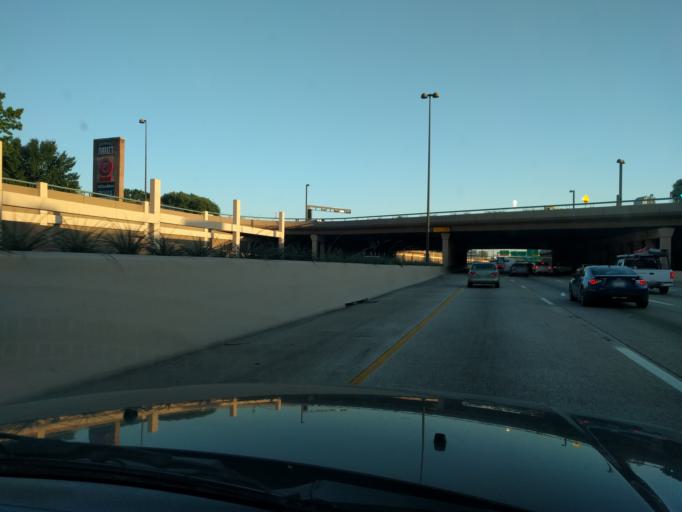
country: US
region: Texas
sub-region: Dallas County
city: Dallas
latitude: 32.8044
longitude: -96.7934
